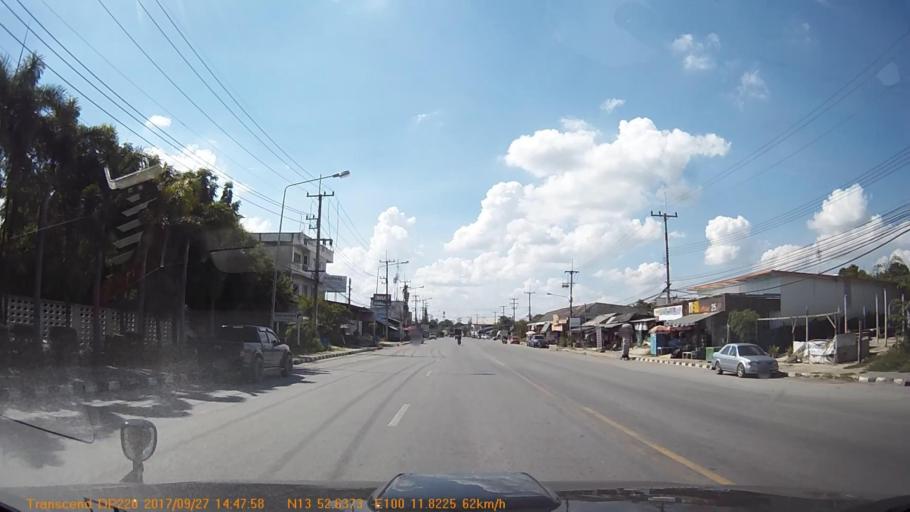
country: TH
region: Nakhon Pathom
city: Nakhon Chai Si
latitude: 13.8773
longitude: 100.1969
